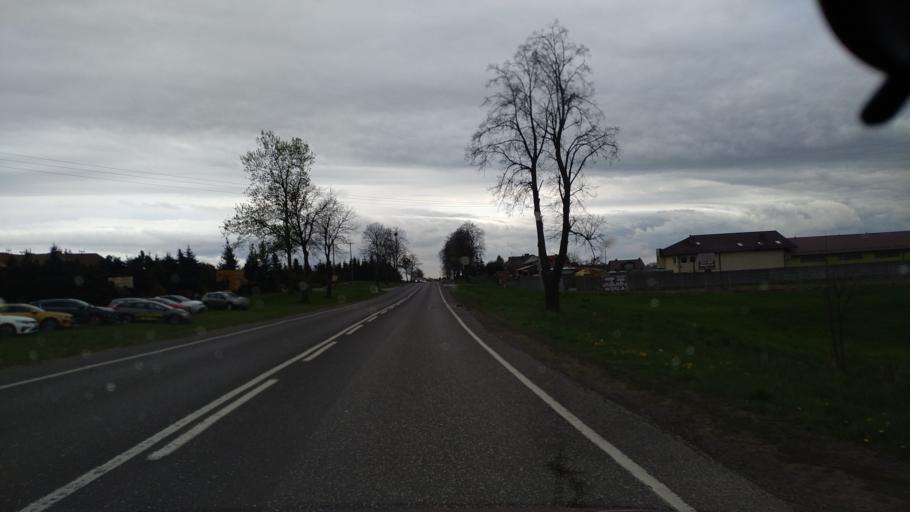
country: PL
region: Pomeranian Voivodeship
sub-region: Powiat starogardzki
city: Starogard Gdanski
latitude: 53.9495
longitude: 18.4729
